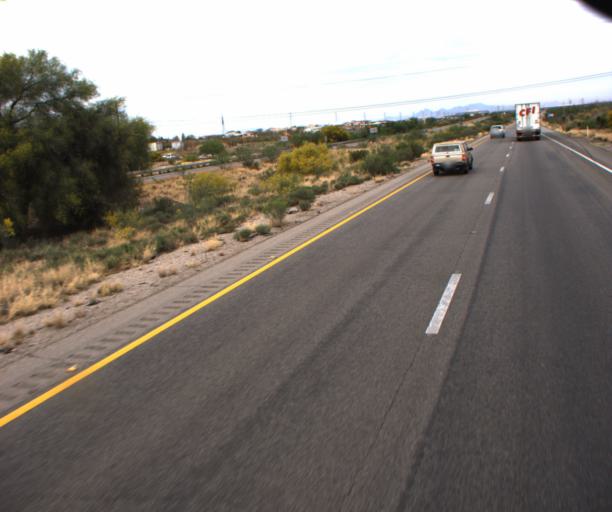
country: US
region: Arizona
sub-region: Pima County
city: Vail
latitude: 32.0123
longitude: -110.6980
